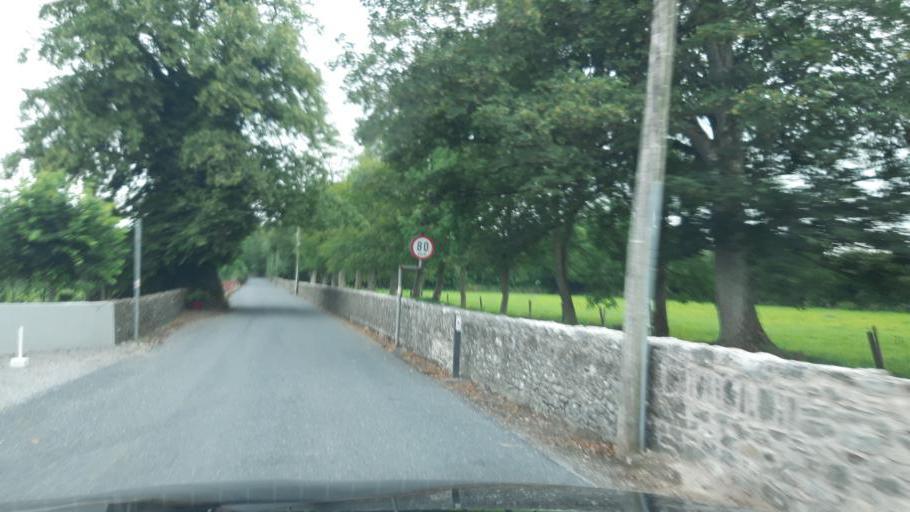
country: IE
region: Leinster
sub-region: Kilkenny
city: Ballyragget
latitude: 52.7302
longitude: -7.3986
